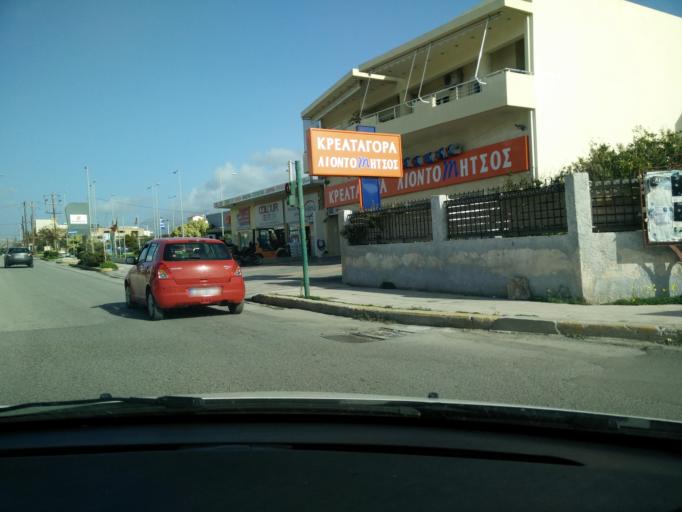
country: GR
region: Crete
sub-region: Nomos Lasithiou
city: Ierapetra
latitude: 35.0149
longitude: 25.7451
